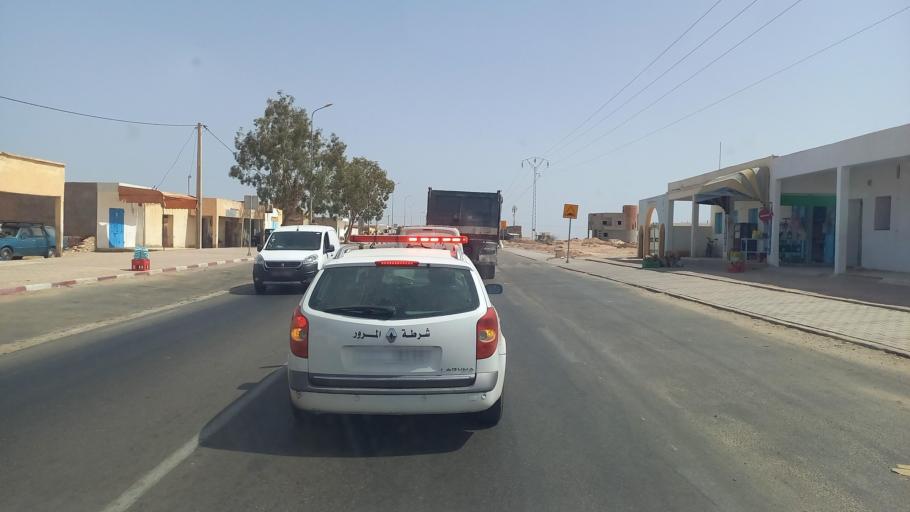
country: TN
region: Madanin
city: Medenine
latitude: 33.3736
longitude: 10.6929
